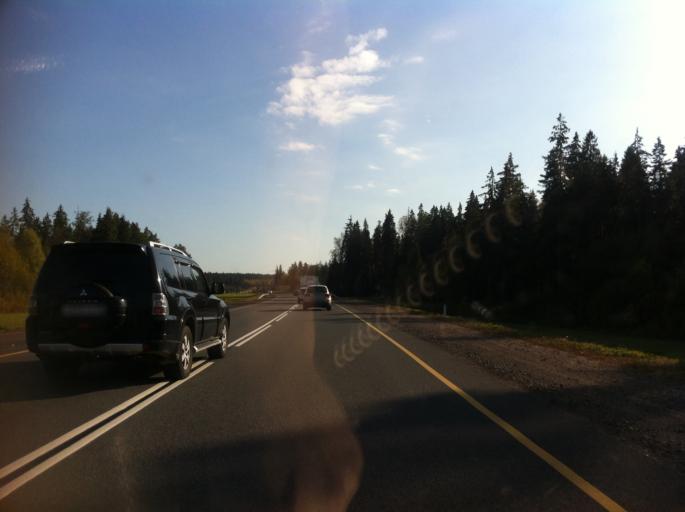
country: RU
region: Leningrad
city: Luga
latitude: 58.7621
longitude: 29.8837
